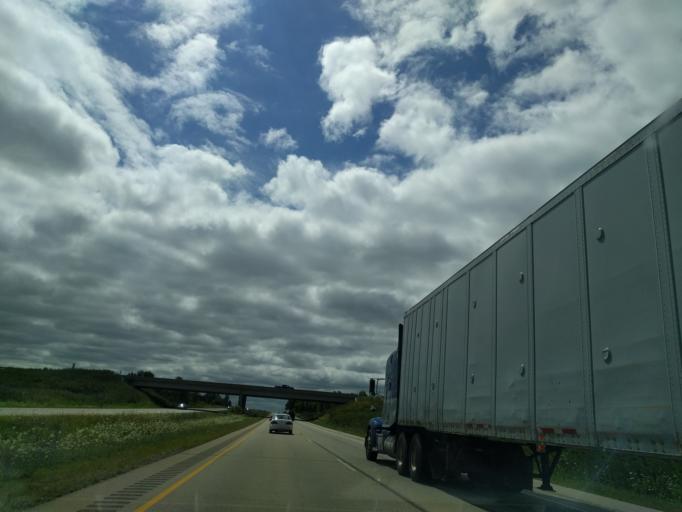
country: US
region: Wisconsin
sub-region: Brown County
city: Suamico
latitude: 44.6789
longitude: -88.0505
